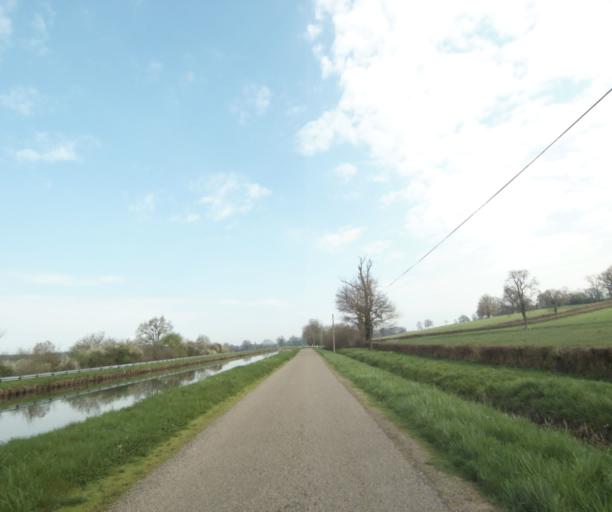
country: FR
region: Bourgogne
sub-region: Departement de Saone-et-Loire
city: Paray-le-Monial
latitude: 46.4835
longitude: 4.1777
